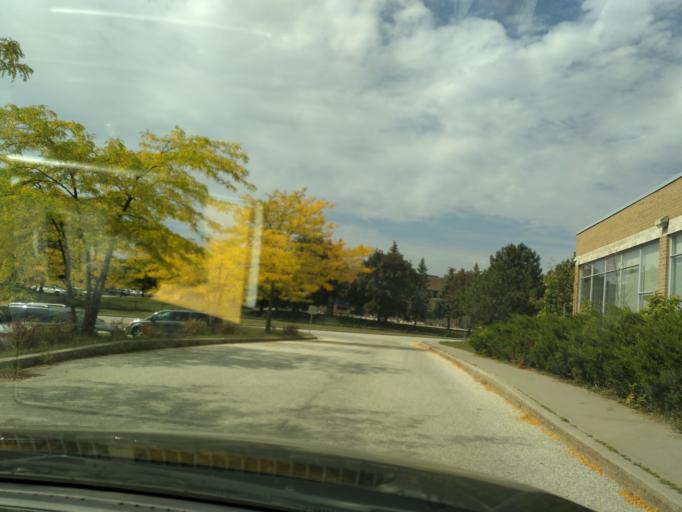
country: CA
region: Ontario
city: Keswick
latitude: 44.2235
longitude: -79.4582
